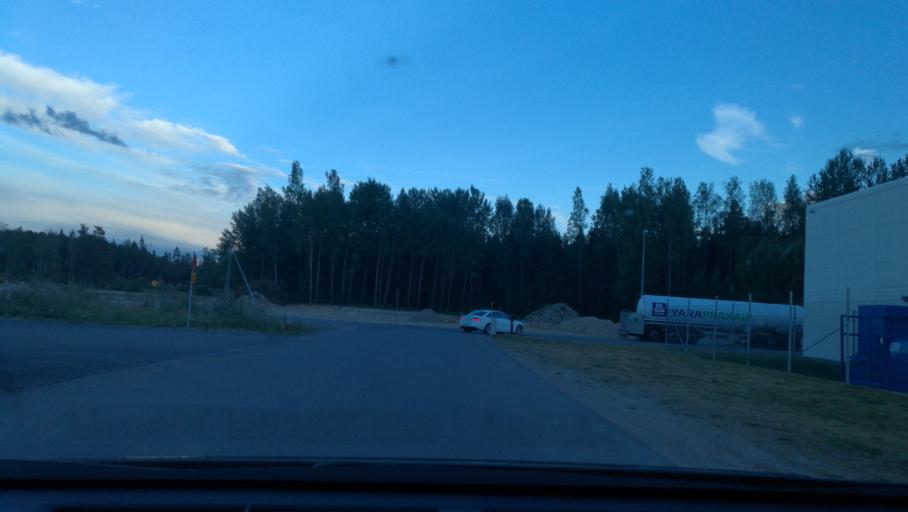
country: SE
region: Soedermanland
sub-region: Katrineholms Kommun
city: Katrineholm
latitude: 59.0068
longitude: 16.2370
